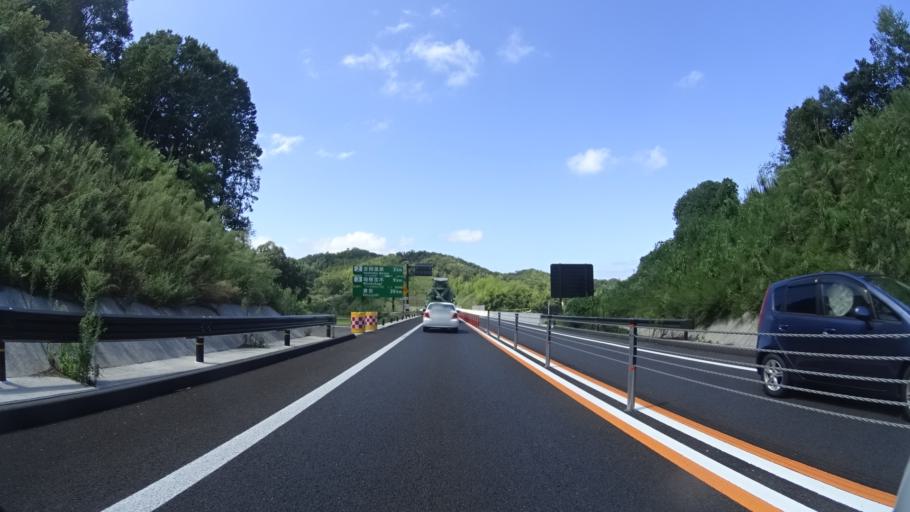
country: JP
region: Tottori
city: Tottori
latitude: 35.4954
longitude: 134.1762
